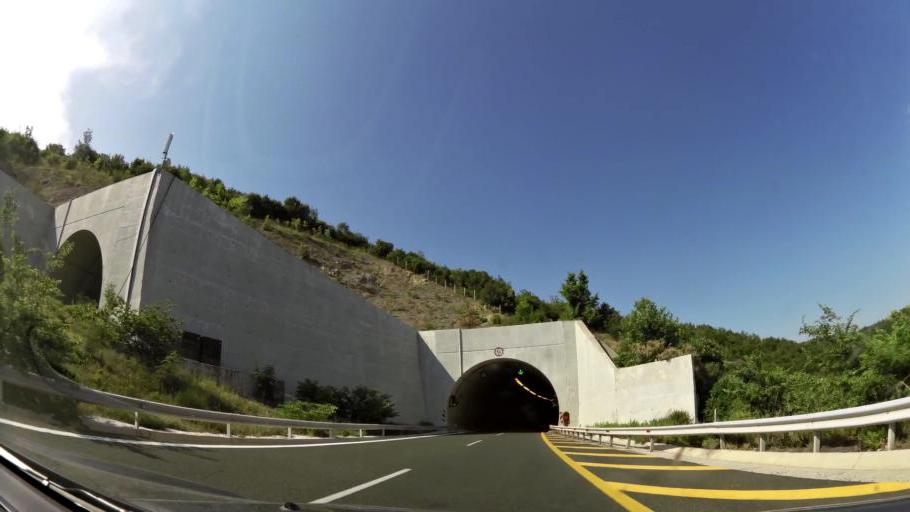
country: GR
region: Central Macedonia
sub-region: Nomos Imathias
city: Veroia
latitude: 40.4380
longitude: 22.1806
